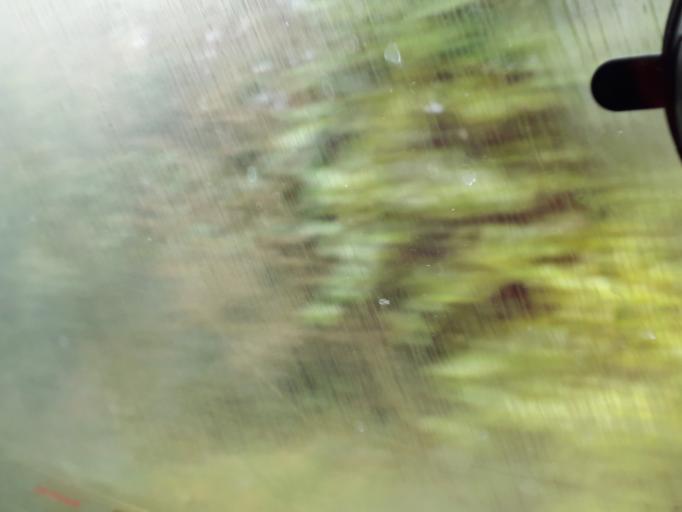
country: IE
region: Leinster
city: Ballyboden
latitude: 53.2576
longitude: -6.3004
